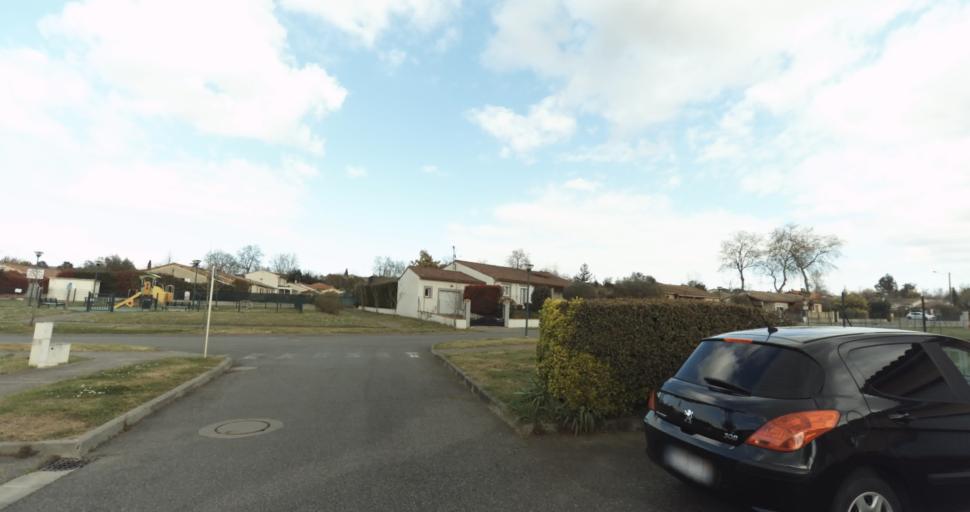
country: FR
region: Midi-Pyrenees
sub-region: Departement de la Haute-Garonne
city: Auterive
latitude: 43.3540
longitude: 1.4833
